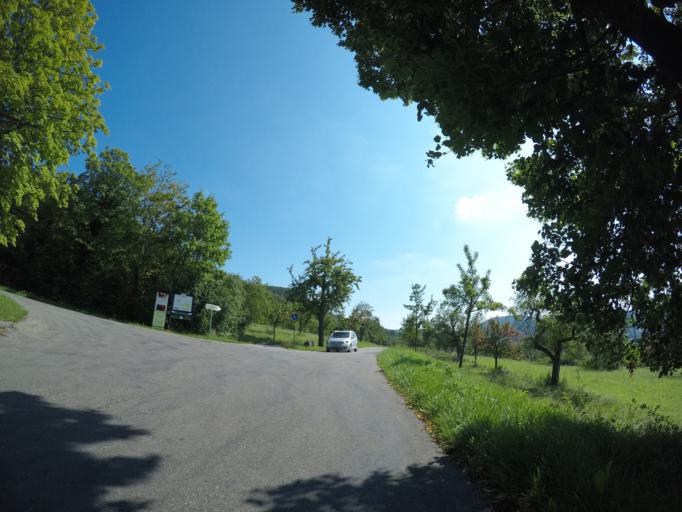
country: DE
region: Baden-Wuerttemberg
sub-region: Tuebingen Region
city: Pfullingen
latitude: 48.4664
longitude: 9.2426
